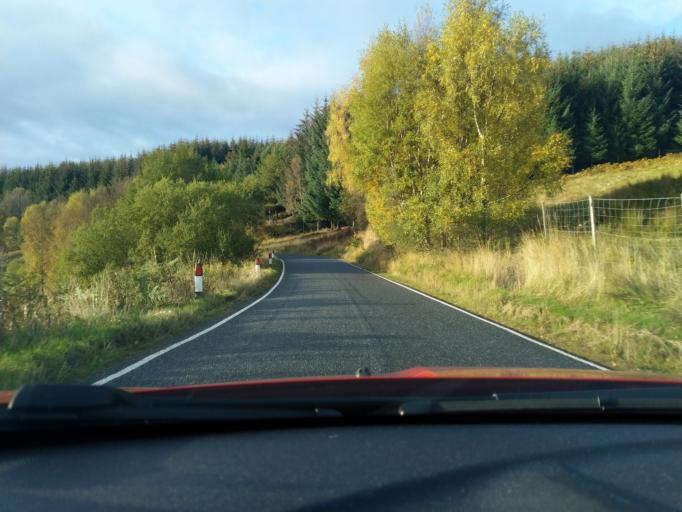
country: GB
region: Scotland
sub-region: Perth and Kinross
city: Aberfeldy
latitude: 56.7271
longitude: -4.1144
